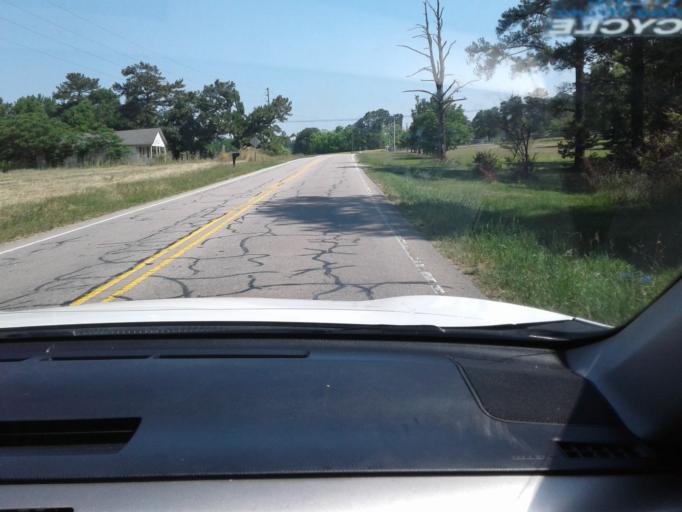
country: US
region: North Carolina
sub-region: Wake County
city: Fuquay-Varina
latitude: 35.5765
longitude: -78.8447
